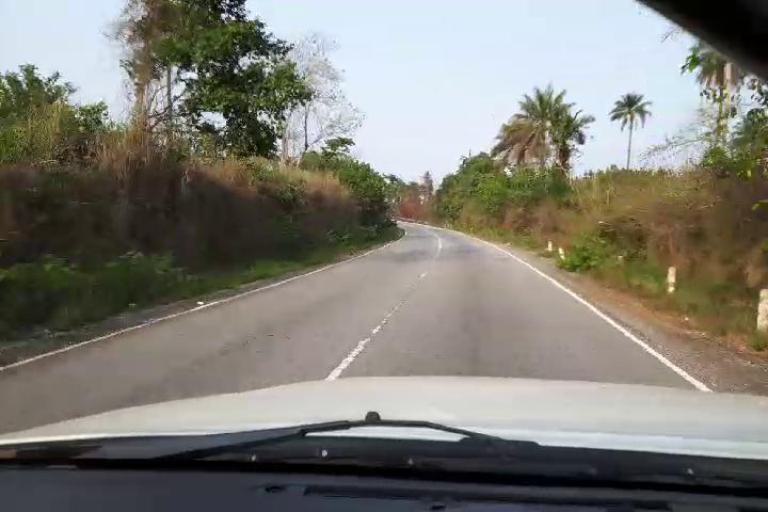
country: SL
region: Eastern Province
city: Blama
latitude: 7.9364
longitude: -11.5110
